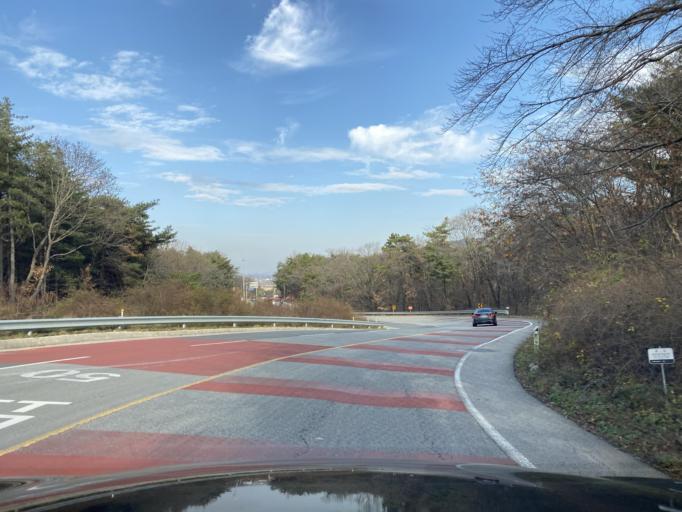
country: KR
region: Chungcheongnam-do
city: Hongsung
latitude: 36.6657
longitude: 126.6357
